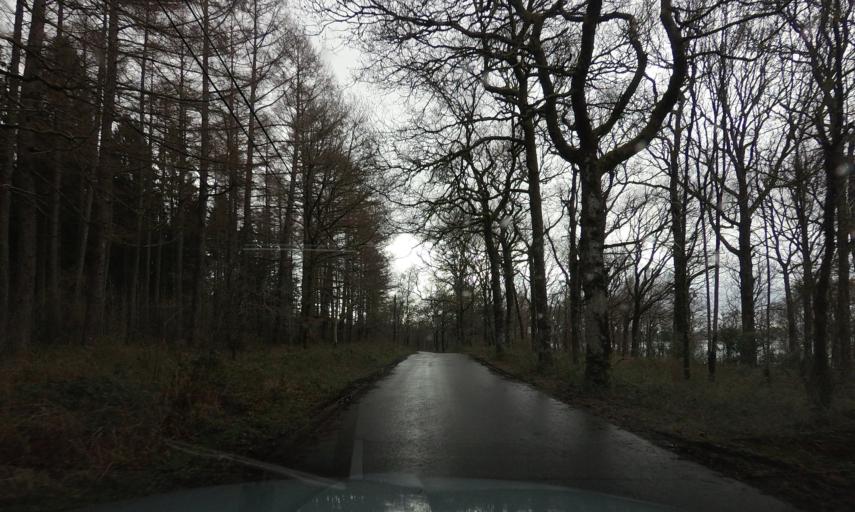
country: GB
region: Scotland
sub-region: West Dunbartonshire
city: Balloch
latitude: 56.1279
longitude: -4.6067
